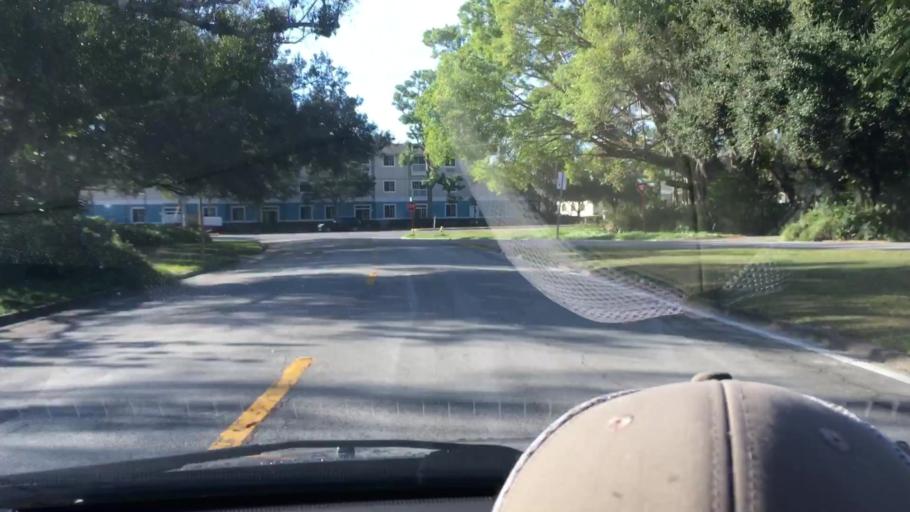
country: US
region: Florida
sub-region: Indian River County
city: Vero Beach
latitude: 27.6390
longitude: -80.4100
